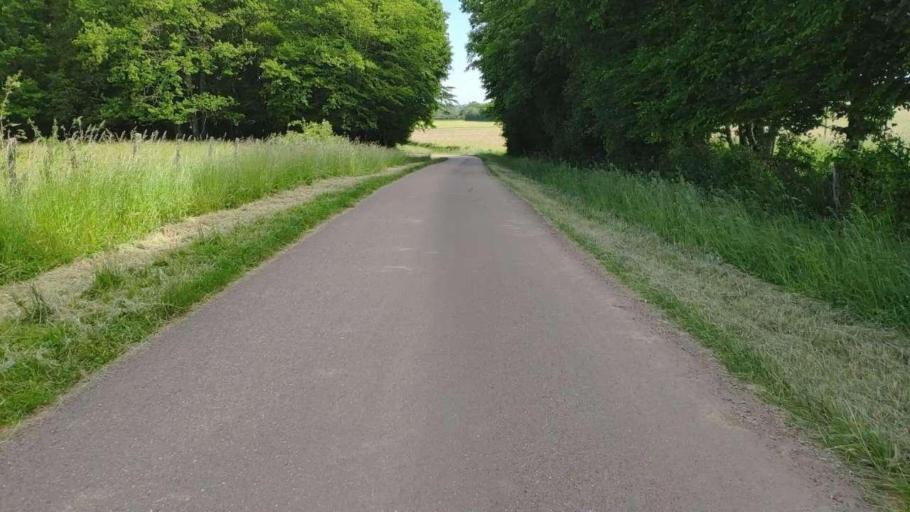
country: FR
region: Franche-Comte
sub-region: Departement du Jura
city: Bletterans
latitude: 46.7156
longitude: 5.4457
